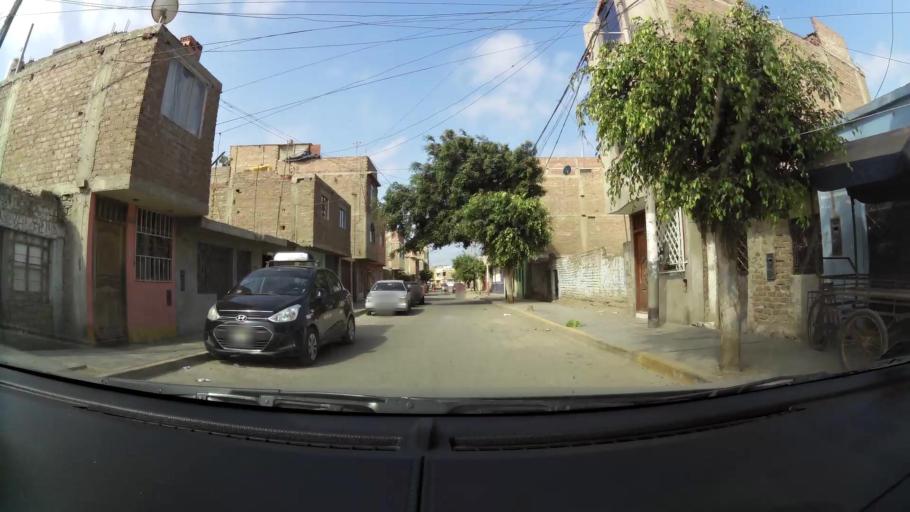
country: PE
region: La Libertad
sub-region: Provincia de Trujillo
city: Trujillo
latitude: -8.1167
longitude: -79.0138
